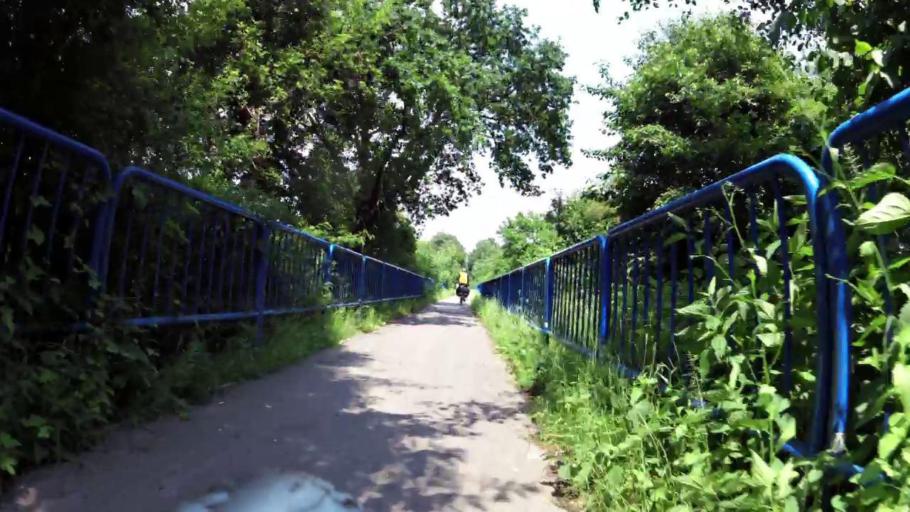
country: PL
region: Kujawsko-Pomorskie
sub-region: Powiat bydgoski
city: Koronowo
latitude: 53.2938
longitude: 17.9477
